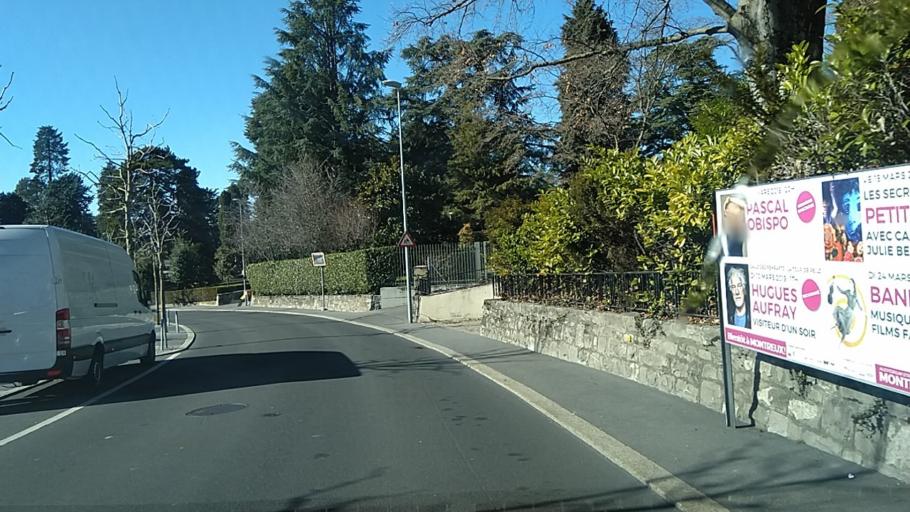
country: CH
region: Vaud
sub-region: Riviera-Pays-d'Enhaut District
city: Le Chatelard
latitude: 46.4429
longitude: 6.9010
